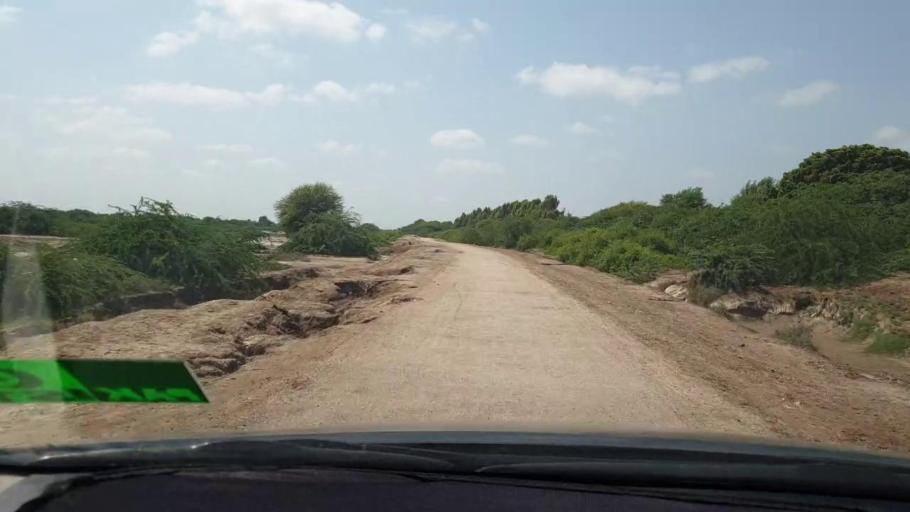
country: PK
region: Sindh
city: Naukot
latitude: 24.8858
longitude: 69.1963
